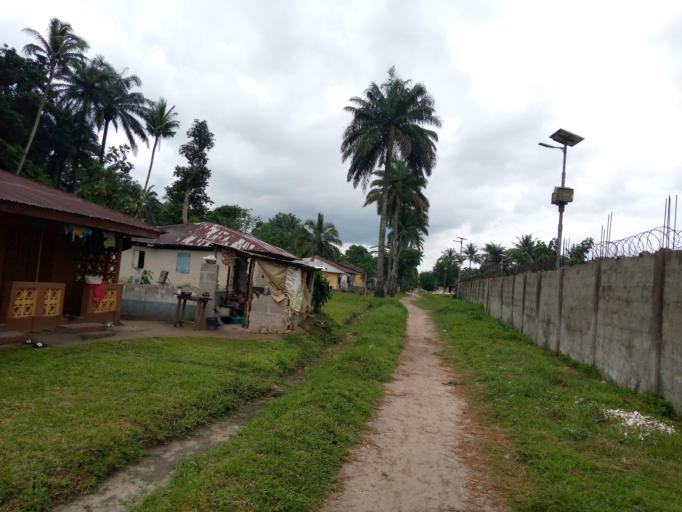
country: SL
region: Southern Province
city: Bonthe
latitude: 7.5298
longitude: -12.5093
